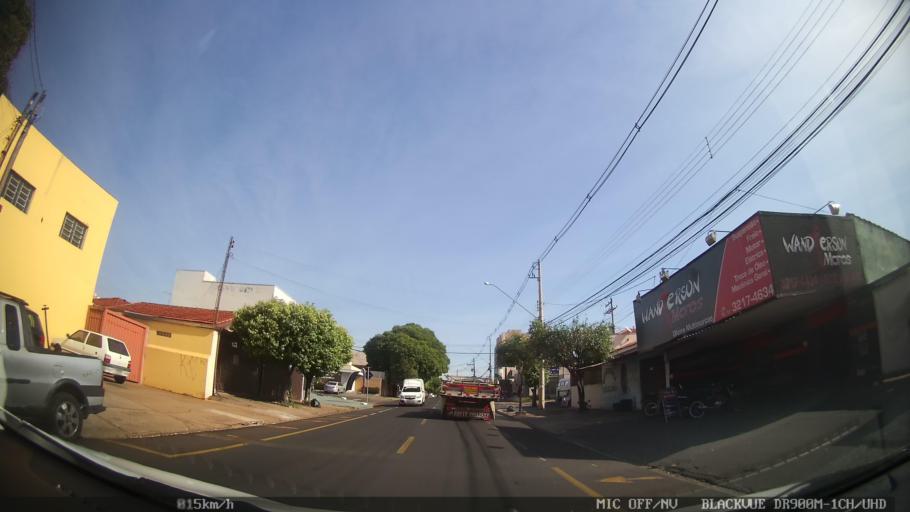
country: BR
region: Sao Paulo
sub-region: Sao Jose Do Rio Preto
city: Sao Jose do Rio Preto
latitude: -20.7946
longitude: -49.4080
